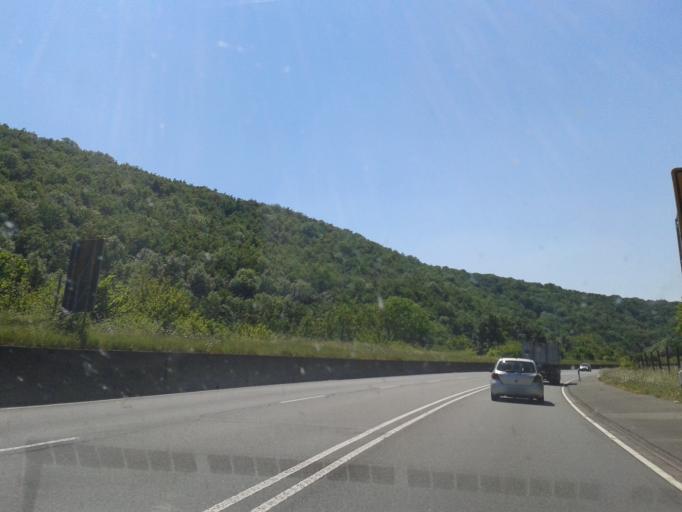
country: DE
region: North Rhine-Westphalia
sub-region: Regierungsbezirk Detmold
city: Schlangen
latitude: 51.8334
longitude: 8.8966
